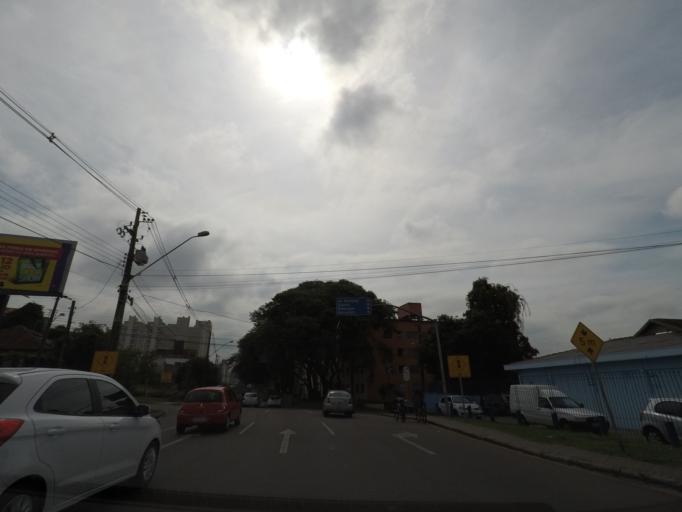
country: BR
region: Parana
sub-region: Curitiba
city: Curitiba
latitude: -25.4766
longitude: -49.2890
